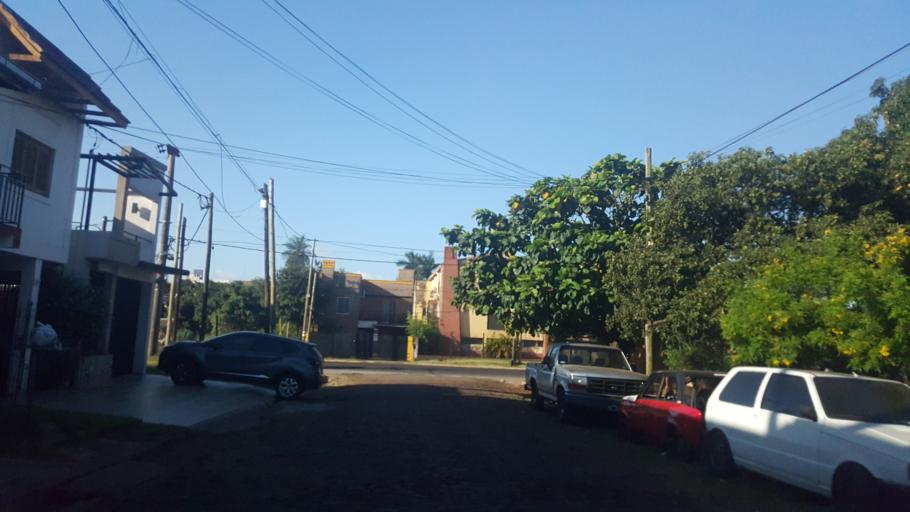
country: AR
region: Misiones
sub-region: Departamento de Capital
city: Posadas
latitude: -27.3820
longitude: -55.8939
